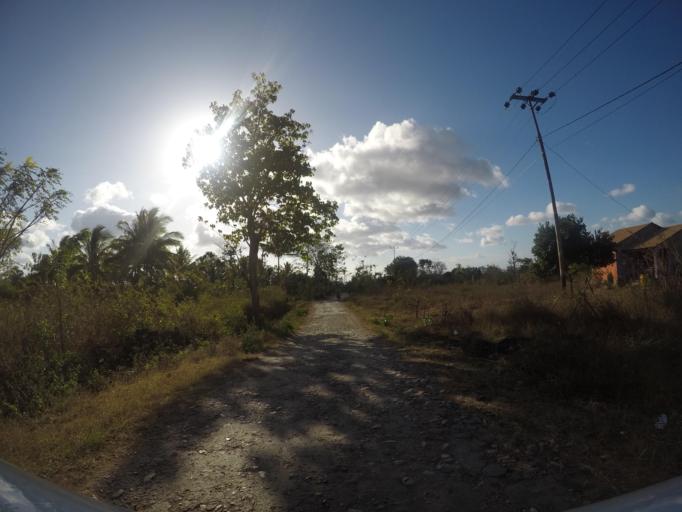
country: TL
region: Lautem
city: Lospalos
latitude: -8.4405
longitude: 126.8615
